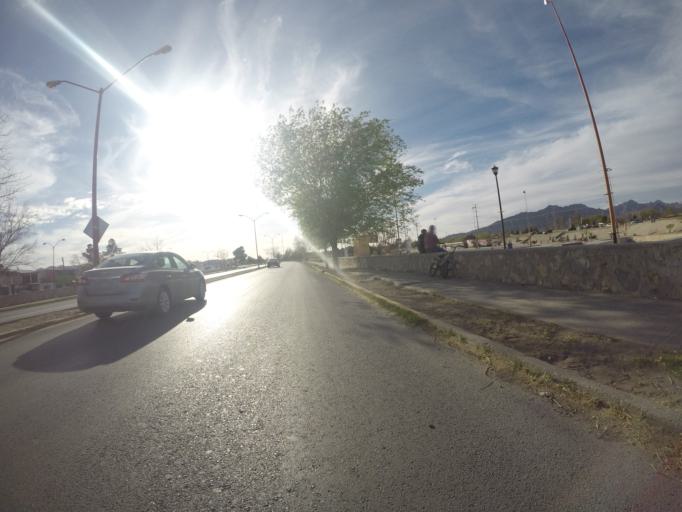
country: US
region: Texas
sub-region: El Paso County
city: El Paso
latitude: 31.7544
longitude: -106.4420
